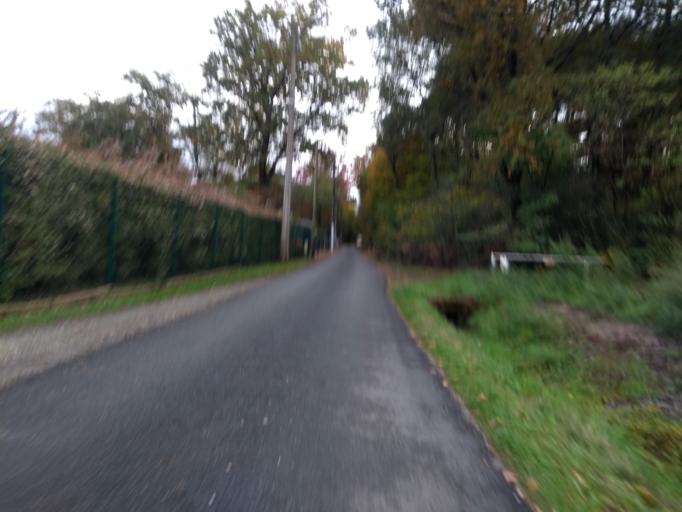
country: FR
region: Aquitaine
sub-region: Departement de la Gironde
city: Canejan
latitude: 44.7661
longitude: -0.6431
